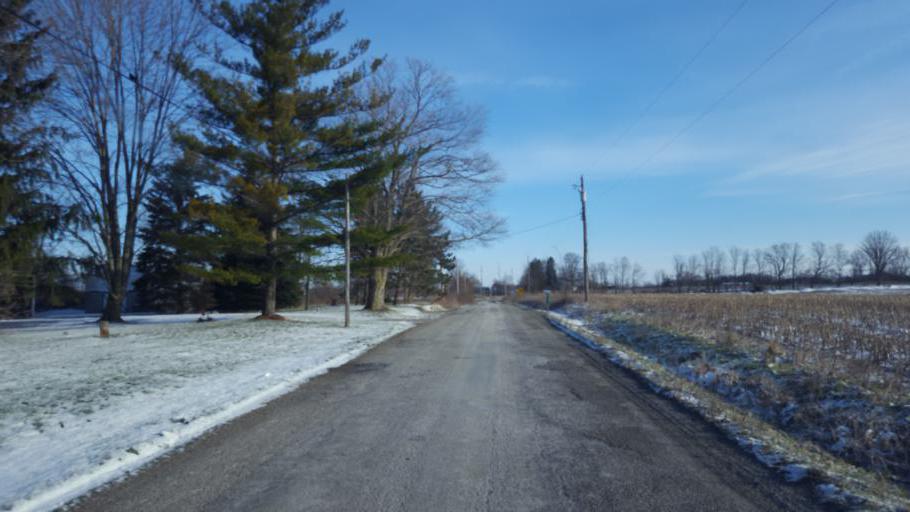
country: US
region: Ohio
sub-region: Morrow County
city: Mount Gilead
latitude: 40.6122
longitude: -82.8420
